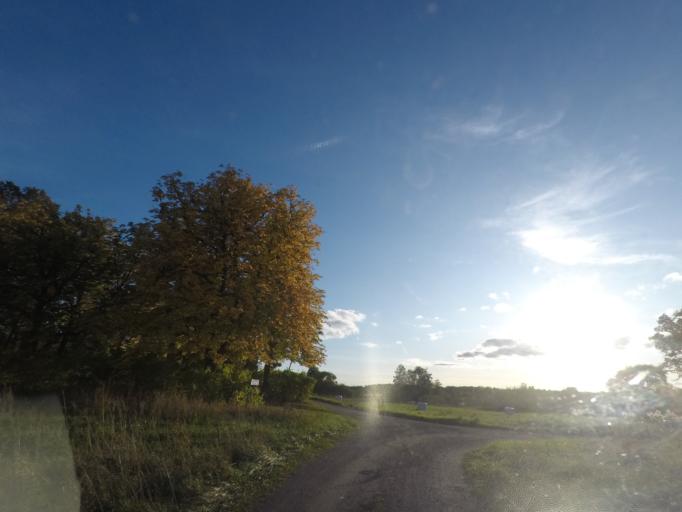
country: SE
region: Vaestmanland
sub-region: Hallstahammars Kommun
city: Kolback
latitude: 59.4790
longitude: 16.2058
